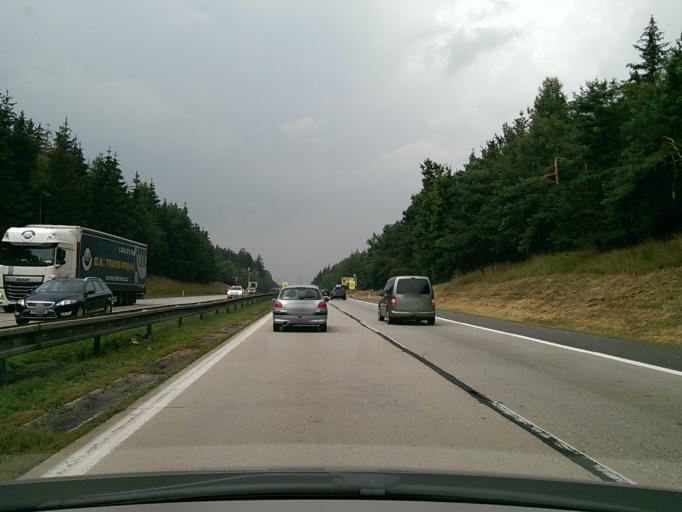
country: CZ
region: Vysocina
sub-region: Okres Zd'ar nad Sazavou
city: Velka Bites
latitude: 49.2714
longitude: 16.2595
